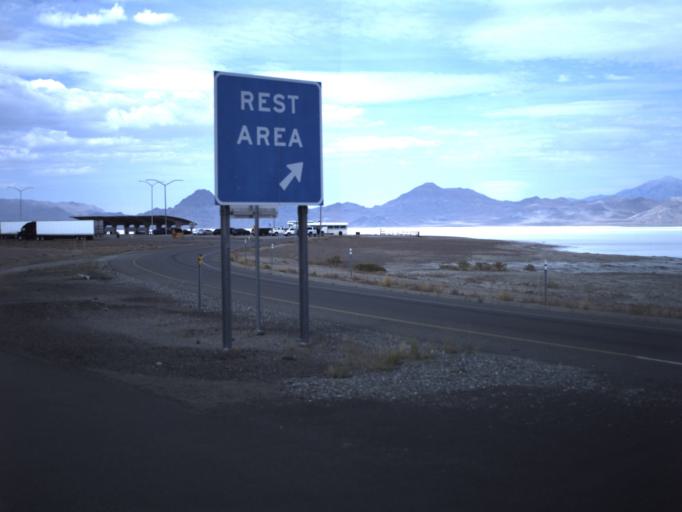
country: US
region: Utah
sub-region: Tooele County
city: Wendover
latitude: 40.7394
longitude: -113.8492
